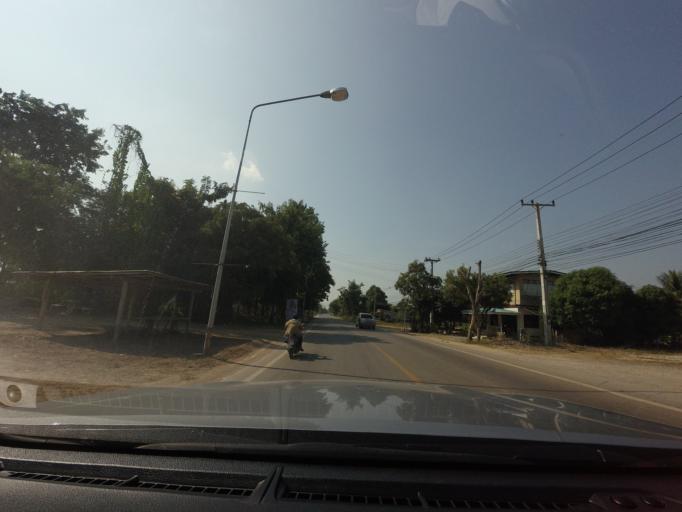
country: TH
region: Phitsanulok
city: Bang Rakam
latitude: 16.8088
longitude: 100.0194
